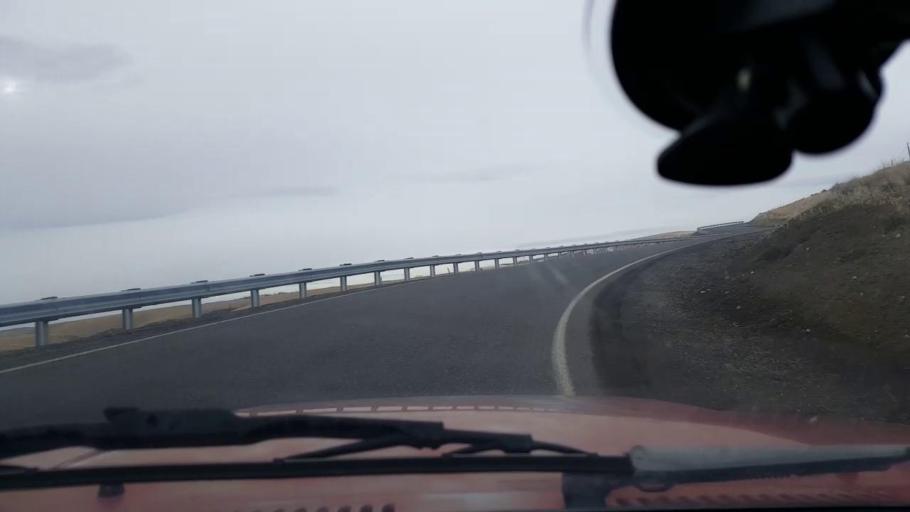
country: US
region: Washington
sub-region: Asotin County
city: Clarkston Heights-Vineland
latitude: 46.3330
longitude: -117.3087
